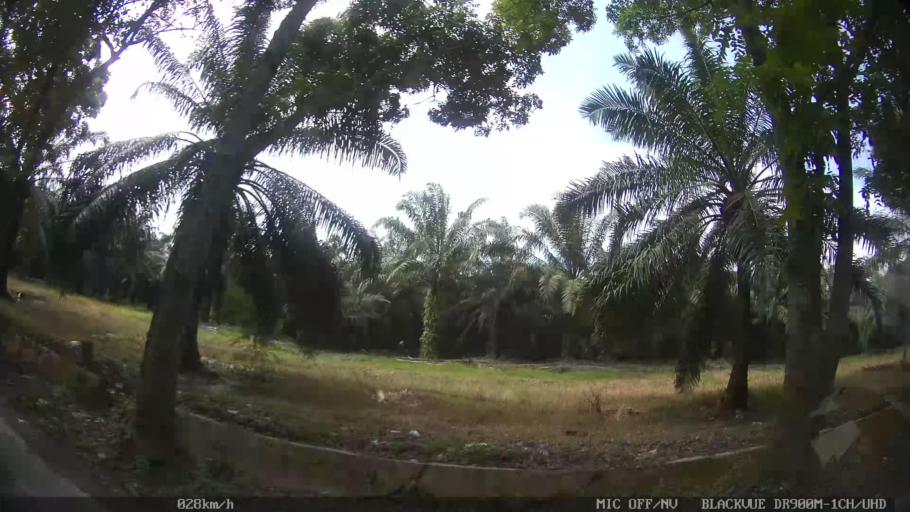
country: ID
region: North Sumatra
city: Binjai
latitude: 3.6512
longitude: 98.5284
